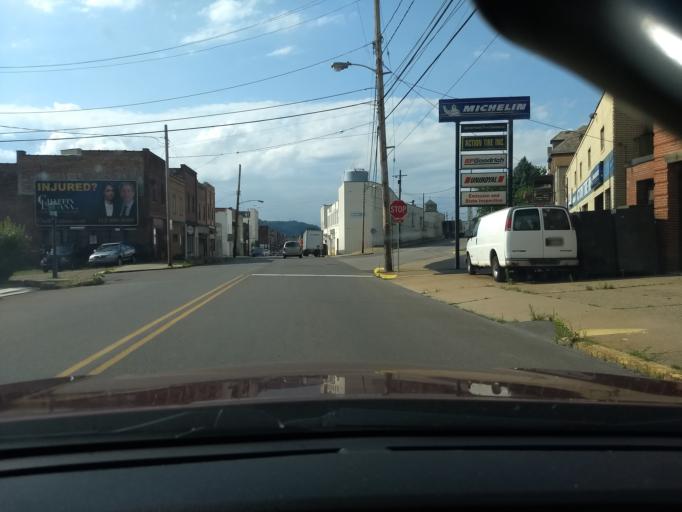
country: US
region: Pennsylvania
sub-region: Beaver County
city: Ambridge
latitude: 40.5820
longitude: -80.2240
